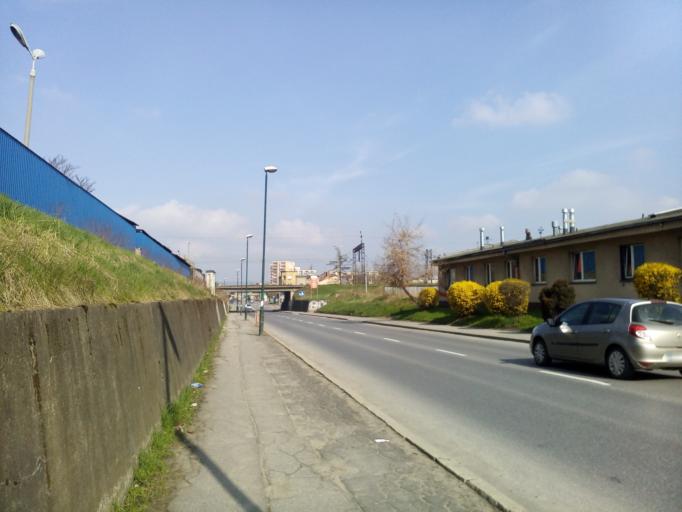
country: PL
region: Lesser Poland Voivodeship
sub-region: Powiat nowosadecki
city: Nowy Sacz
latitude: 49.6076
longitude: 20.7099
